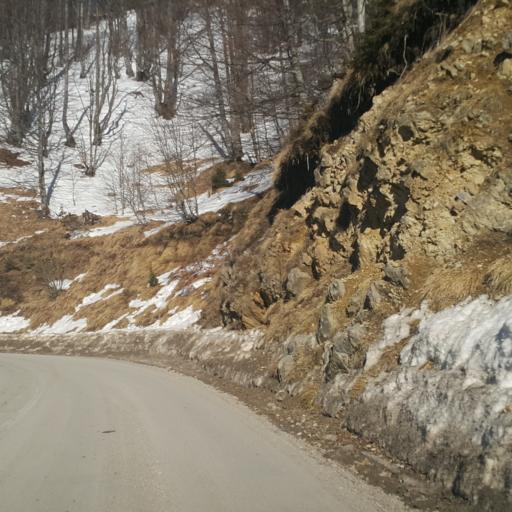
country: XK
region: Mitrovica
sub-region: Komuna e Leposaviqit
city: Leposaviq
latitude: 43.3145
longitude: 20.8589
